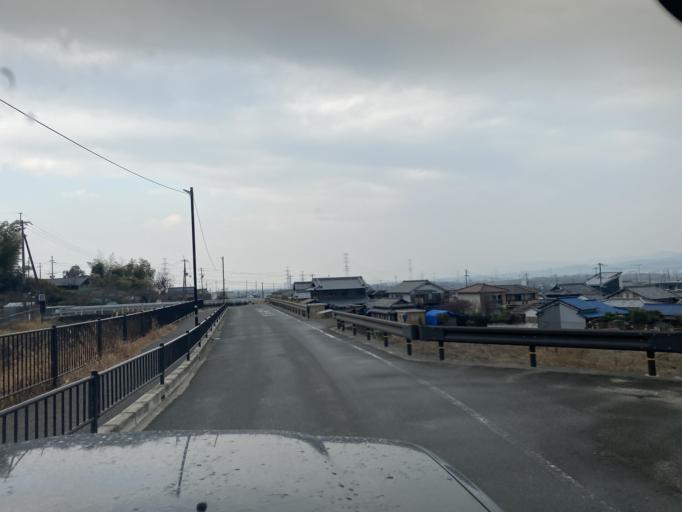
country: JP
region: Kyoto
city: Tanabe
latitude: 34.8223
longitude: 135.7540
